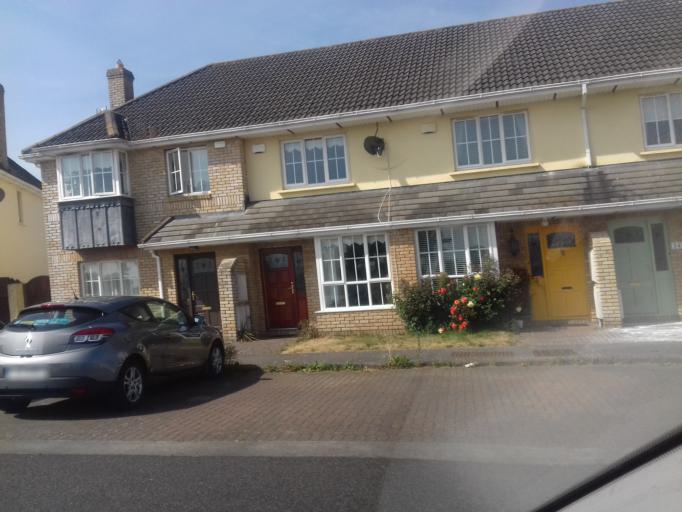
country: IE
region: Leinster
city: Lusk
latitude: 53.5255
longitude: -6.1747
